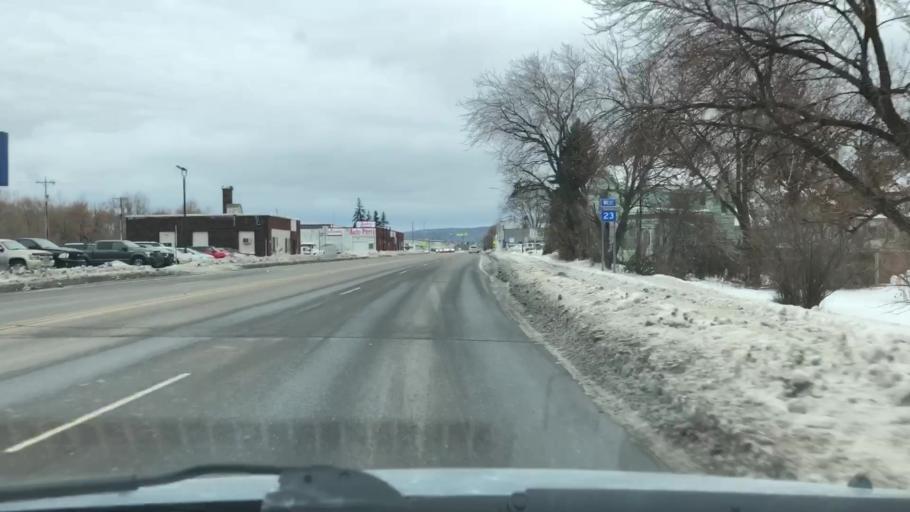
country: US
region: Minnesota
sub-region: Saint Louis County
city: Proctor
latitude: 46.7348
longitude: -92.1751
